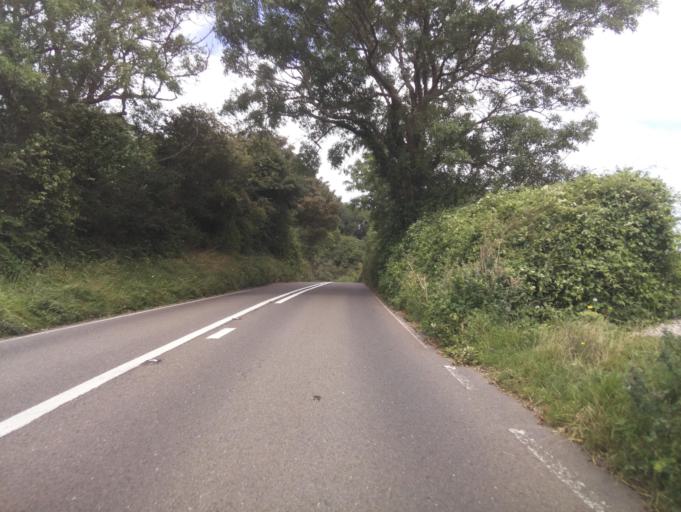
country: GB
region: England
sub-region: Devon
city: Teignmouth
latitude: 50.5266
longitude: -3.5091
